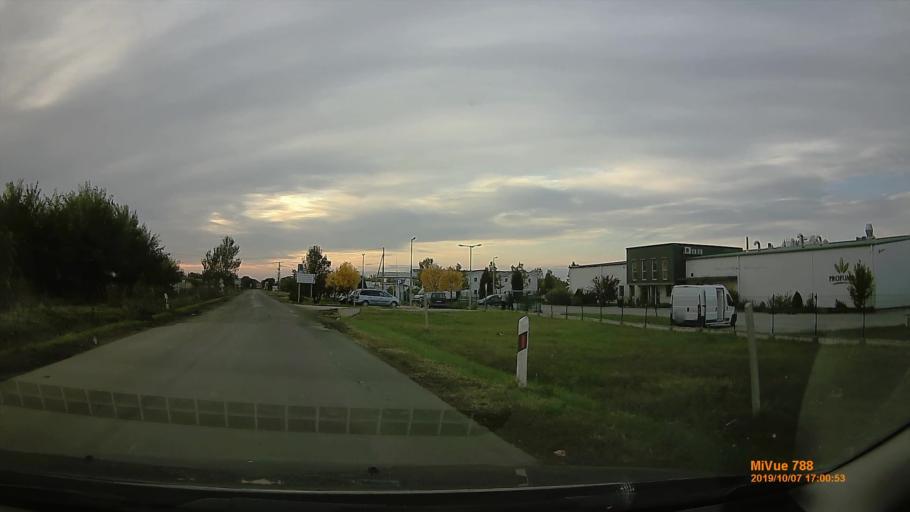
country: HU
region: Bekes
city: Szarvas
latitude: 46.8503
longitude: 20.5692
